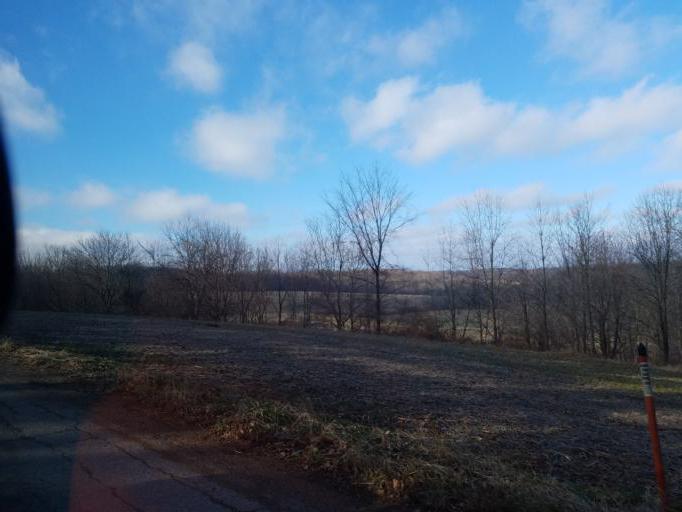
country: US
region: Ohio
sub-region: Sandusky County
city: Bellville
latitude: 40.5727
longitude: -82.5210
